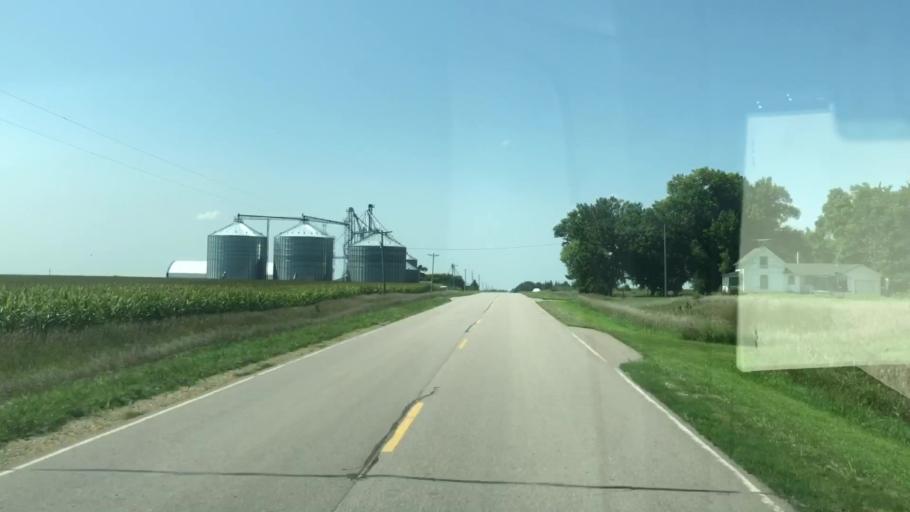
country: US
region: Iowa
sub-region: O'Brien County
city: Sheldon
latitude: 43.2443
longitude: -95.7704
